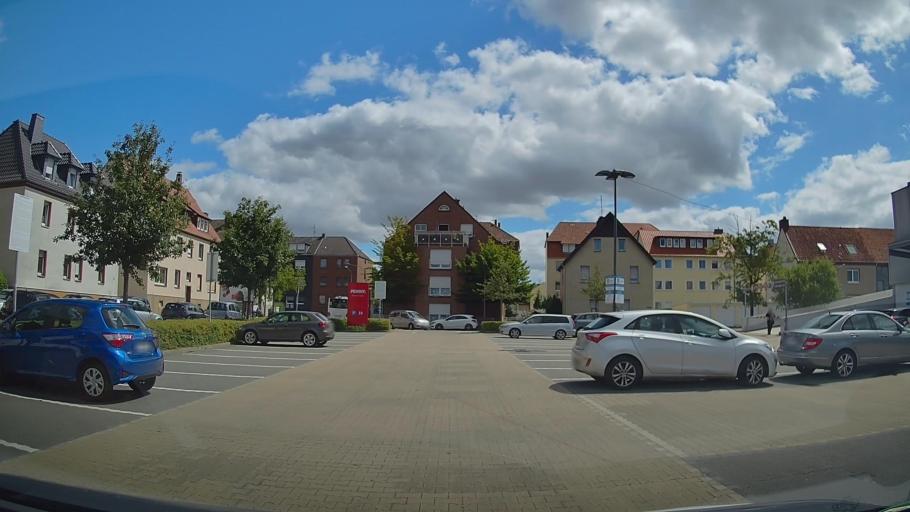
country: DE
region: Lower Saxony
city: Osnabrueck
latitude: 52.2757
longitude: 8.0743
